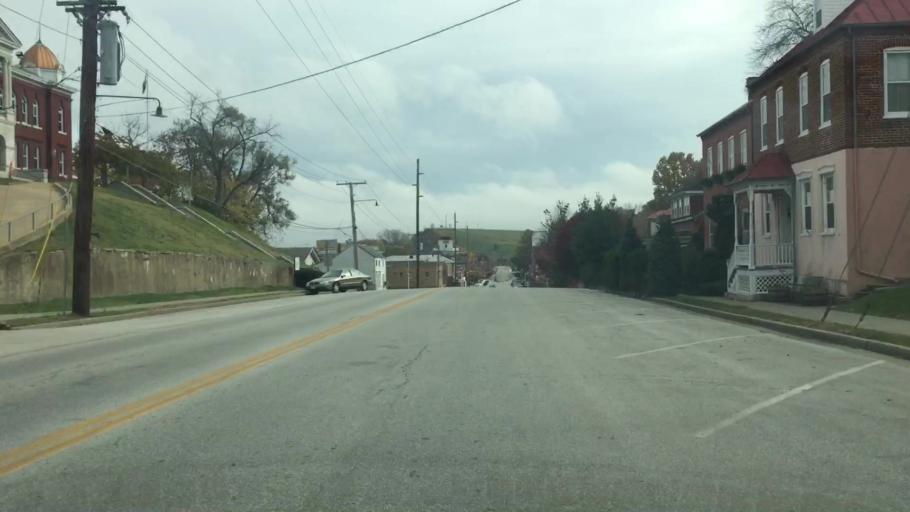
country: US
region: Missouri
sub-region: Gasconade County
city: Hermann
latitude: 38.7070
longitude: -91.4371
